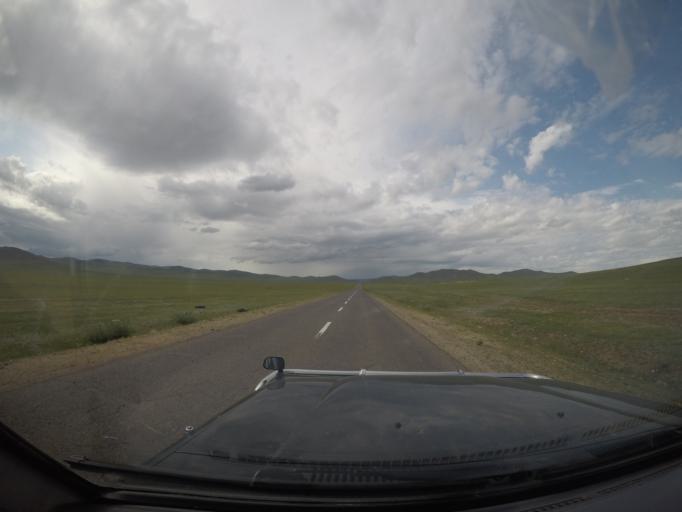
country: MN
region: Hentiy
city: Modot
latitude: 47.6356
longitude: 109.1611
